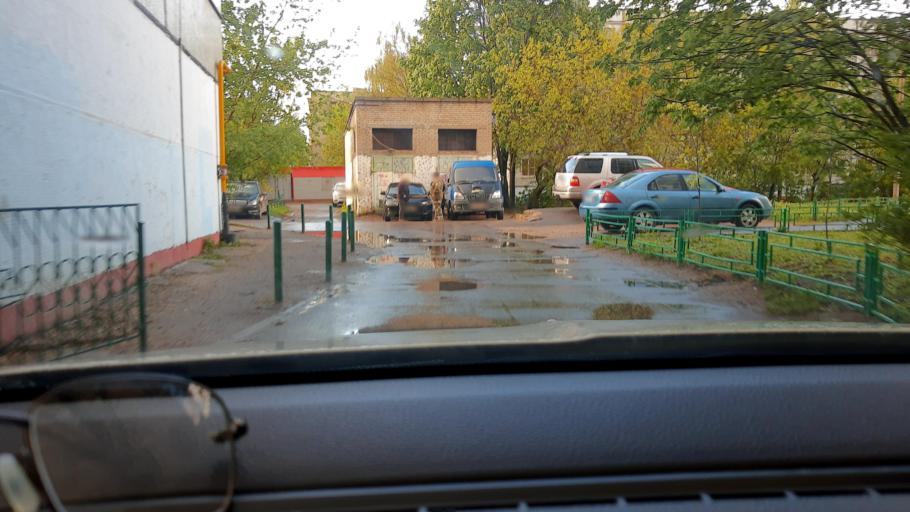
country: RU
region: Moskovskaya
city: Nakhabino
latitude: 55.8385
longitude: 37.1790
